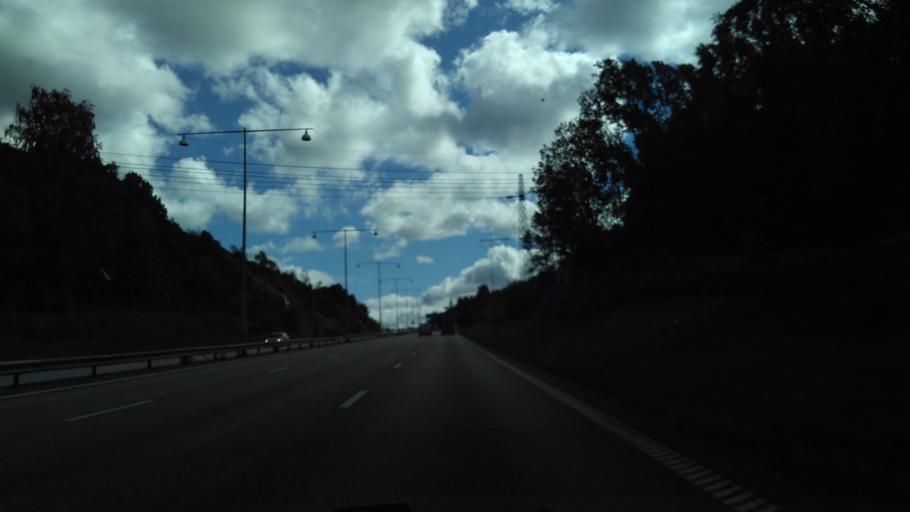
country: SE
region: Vaestra Goetaland
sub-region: Molndal
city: Moelndal
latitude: 57.6814
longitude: 12.0183
